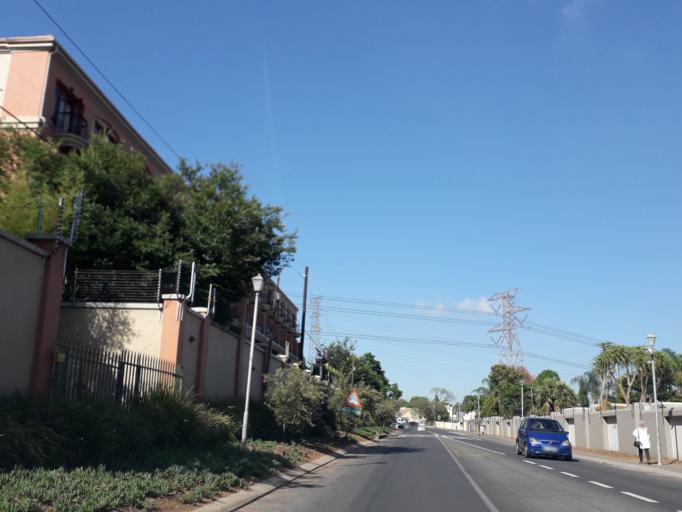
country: ZA
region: Gauteng
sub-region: City of Johannesburg Metropolitan Municipality
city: Modderfontein
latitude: -26.0866
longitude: 28.0608
